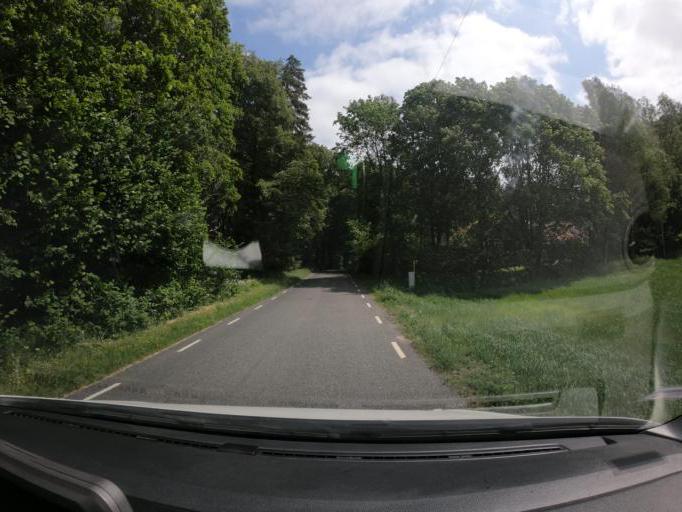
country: SE
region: Skane
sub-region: Hassleholms Kommun
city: Sosdala
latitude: 56.0493
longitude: 13.6464
